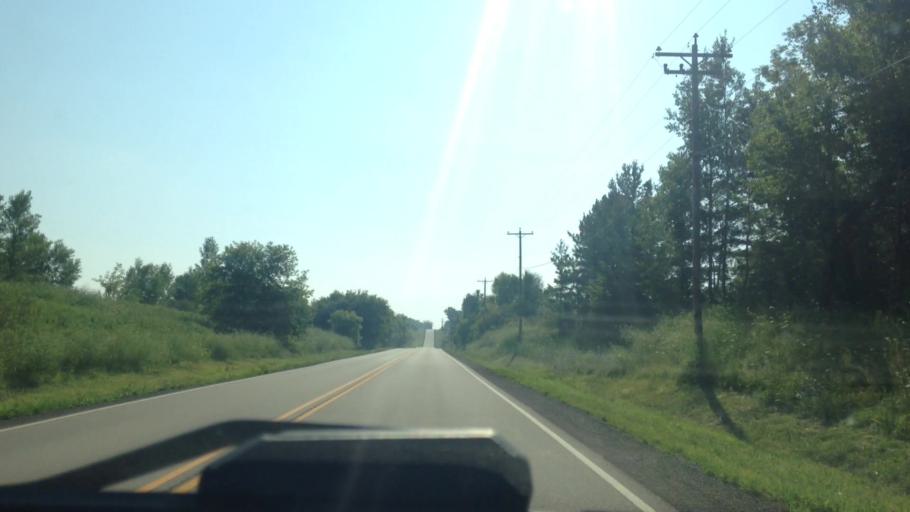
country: US
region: Wisconsin
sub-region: Waukesha County
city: Merton
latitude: 43.1631
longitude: -88.2798
